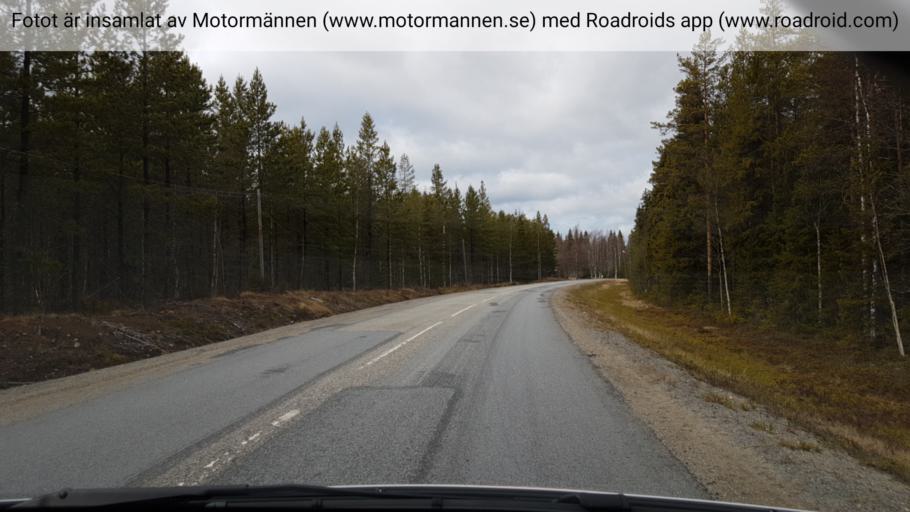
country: SE
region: Vaesterbotten
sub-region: Lycksele Kommun
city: Lycksele
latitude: 64.0607
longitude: 18.4050
